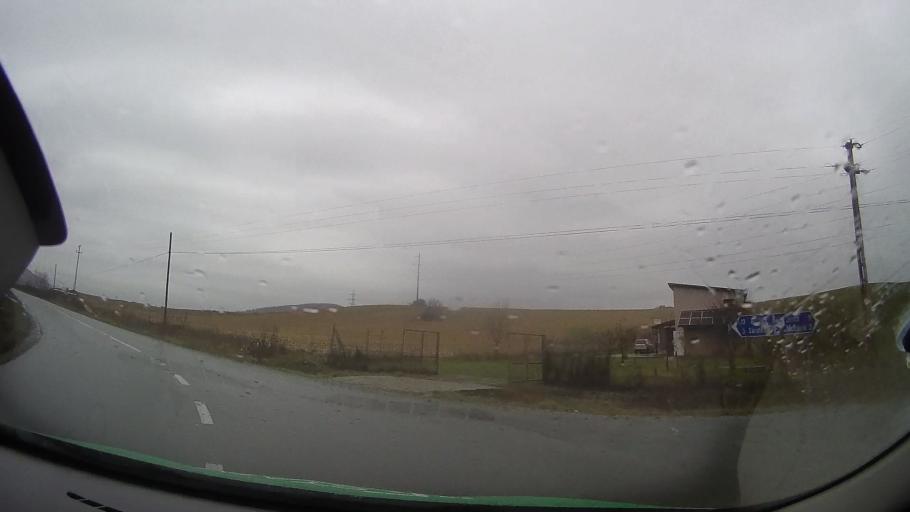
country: RO
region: Bistrita-Nasaud
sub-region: Municipiul Bistrita
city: Viisoara
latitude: 47.0567
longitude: 24.4498
